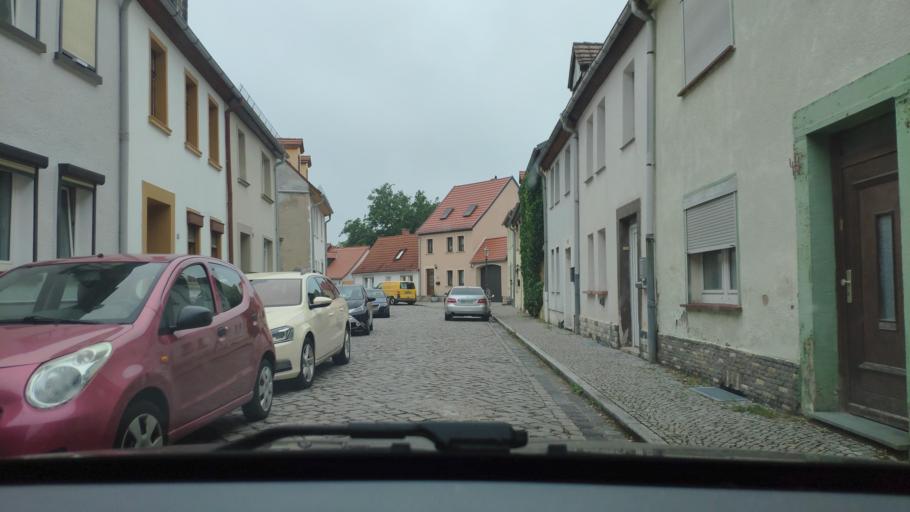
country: DE
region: Saxony-Anhalt
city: Bernburg
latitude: 51.8031
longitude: 11.7335
